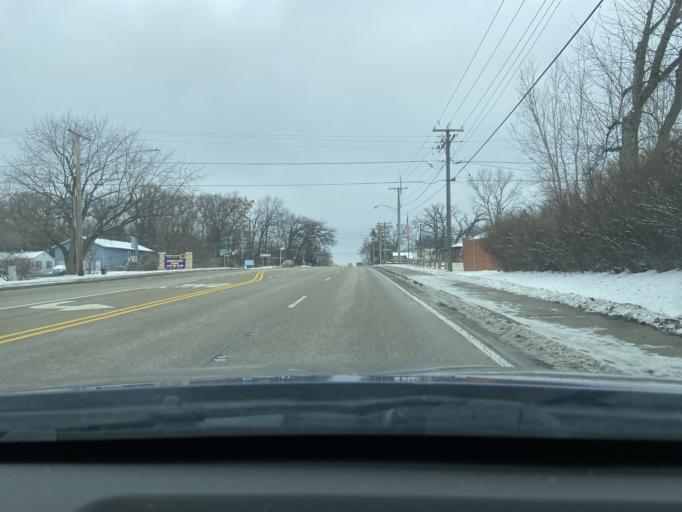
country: US
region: Illinois
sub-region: Lake County
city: Round Lake Beach
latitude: 42.3625
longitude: -88.0898
